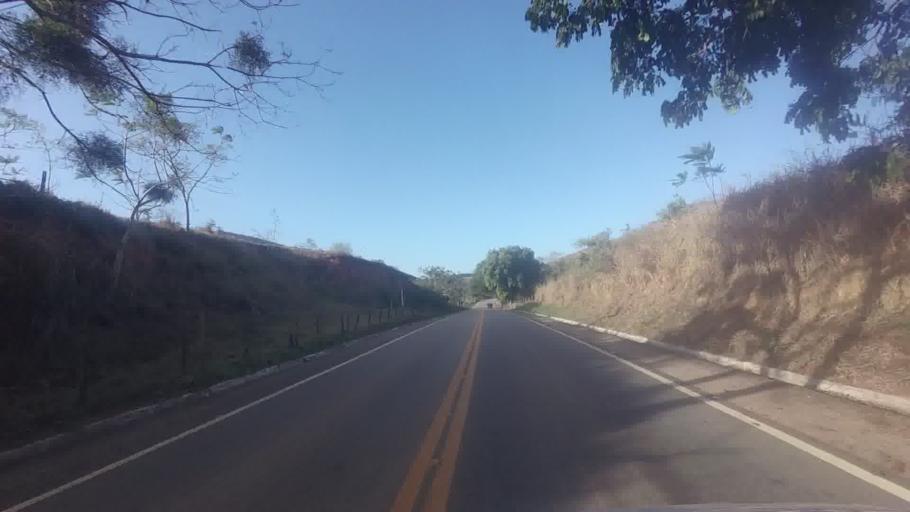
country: BR
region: Espirito Santo
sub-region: Jeronimo Monteiro
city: Jeronimo Monteiro
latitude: -20.9024
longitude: -41.2921
